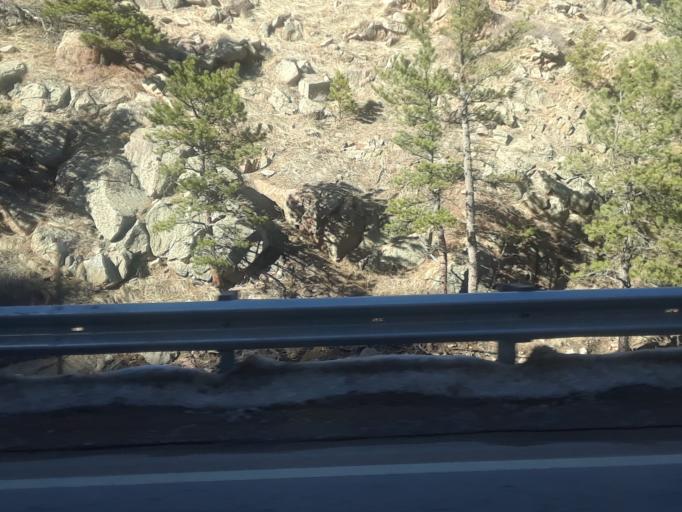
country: US
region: Colorado
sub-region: Boulder County
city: Boulder
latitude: 40.1093
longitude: -105.3114
